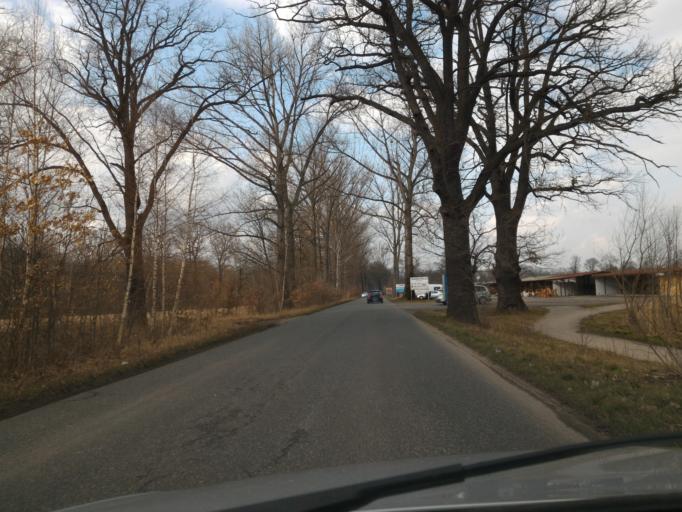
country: DE
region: Saxony
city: Zittau
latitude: 50.8784
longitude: 14.8235
